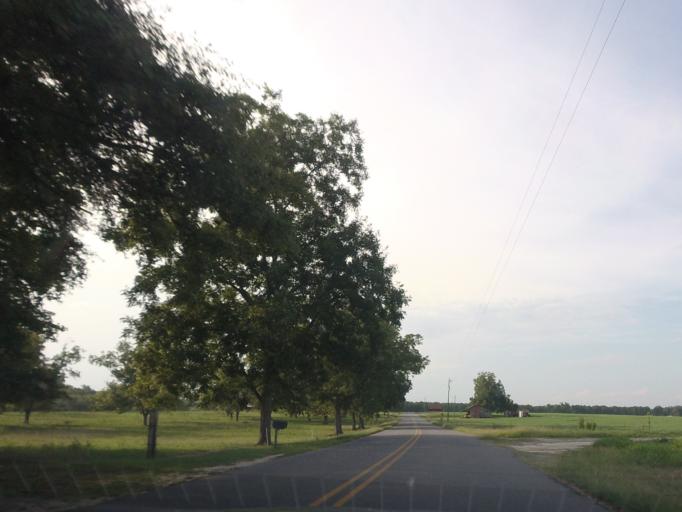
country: US
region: Georgia
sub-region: Bleckley County
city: Cochran
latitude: 32.5246
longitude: -83.3073
